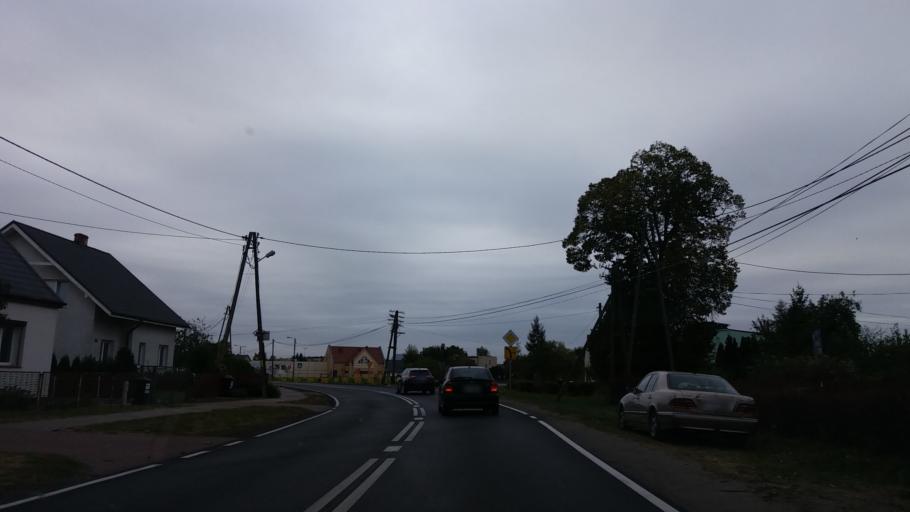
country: PL
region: Lubusz
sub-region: Powiat gorzowski
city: Klodawa
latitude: 52.7857
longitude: 15.2142
